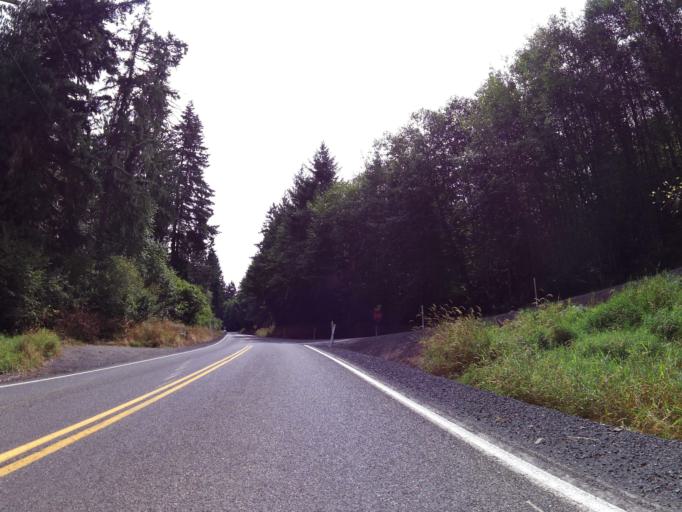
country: US
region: Washington
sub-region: Lewis County
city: Napavine
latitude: 46.5469
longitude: -122.9544
